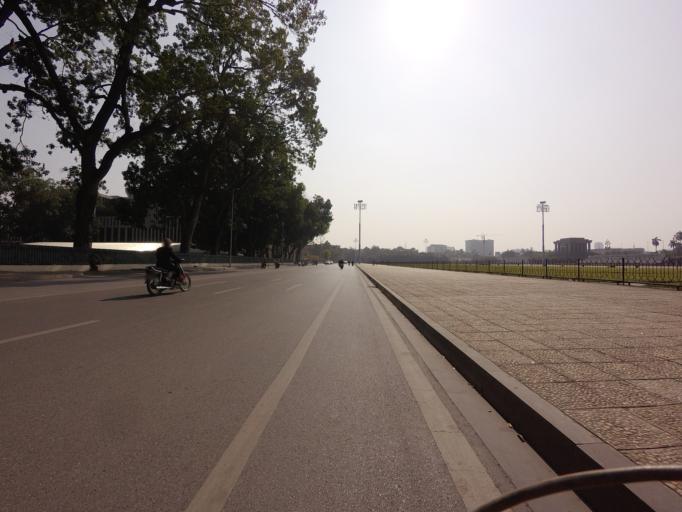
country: VN
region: Ha Noi
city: Hanoi
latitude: 21.0387
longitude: 105.8369
